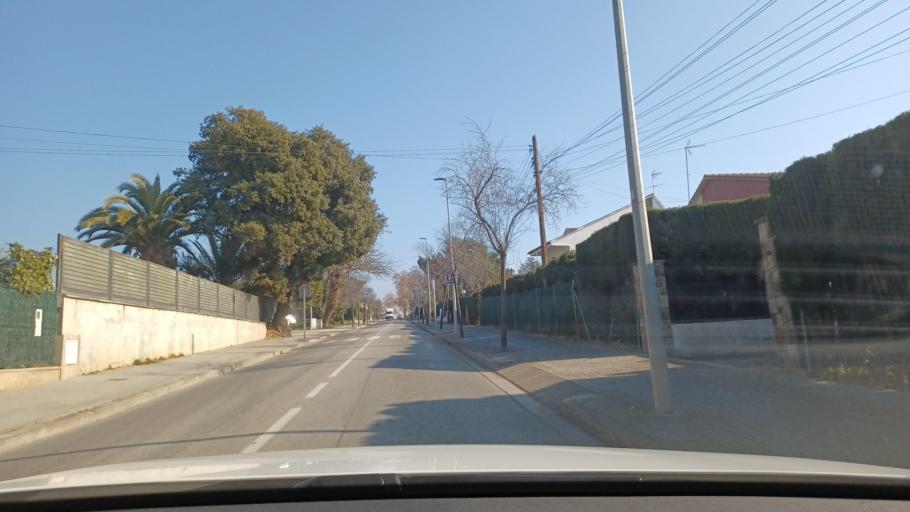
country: ES
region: Catalonia
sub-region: Provincia de Barcelona
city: L'Ametlla del Valles
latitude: 41.6646
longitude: 2.2554
